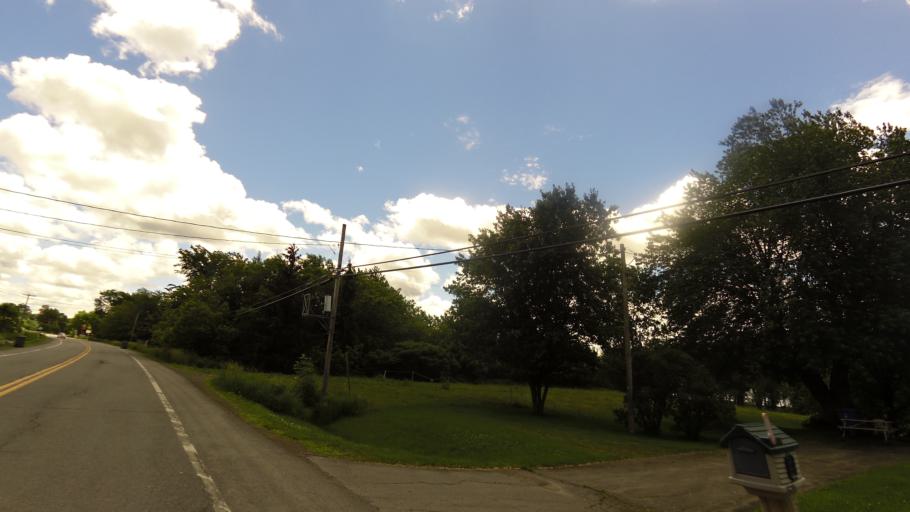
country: CA
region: Quebec
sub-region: Monteregie
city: Hudson
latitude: 45.4952
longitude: -74.1386
